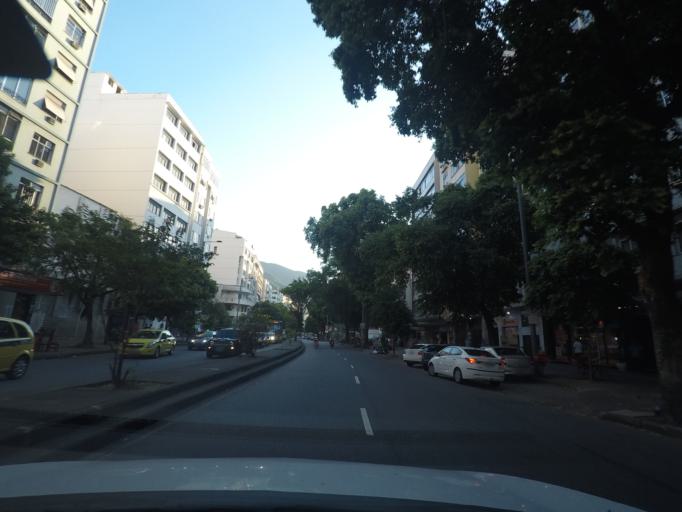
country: BR
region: Rio de Janeiro
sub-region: Rio De Janeiro
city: Rio de Janeiro
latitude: -22.9281
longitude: -43.2364
